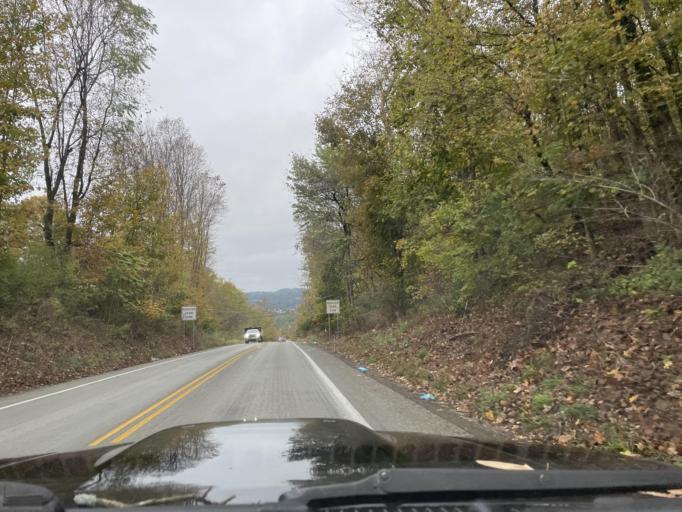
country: US
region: Pennsylvania
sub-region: Allegheny County
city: Springdale
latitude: 40.5323
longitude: -79.7689
